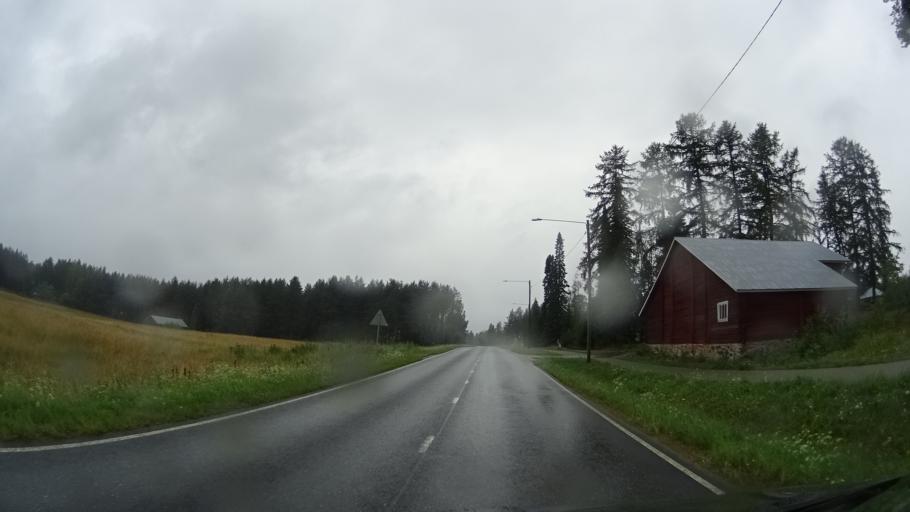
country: FI
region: North Karelia
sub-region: Keski-Karjala
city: Raeaekkylae
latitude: 62.3161
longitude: 29.6166
